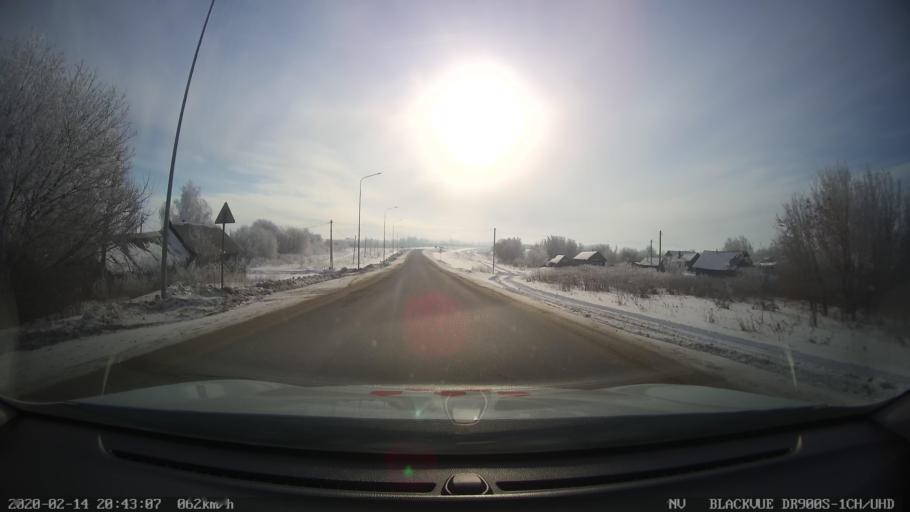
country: RU
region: Tatarstan
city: Kuybyshevskiy Zaton
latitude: 55.3114
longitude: 49.1452
